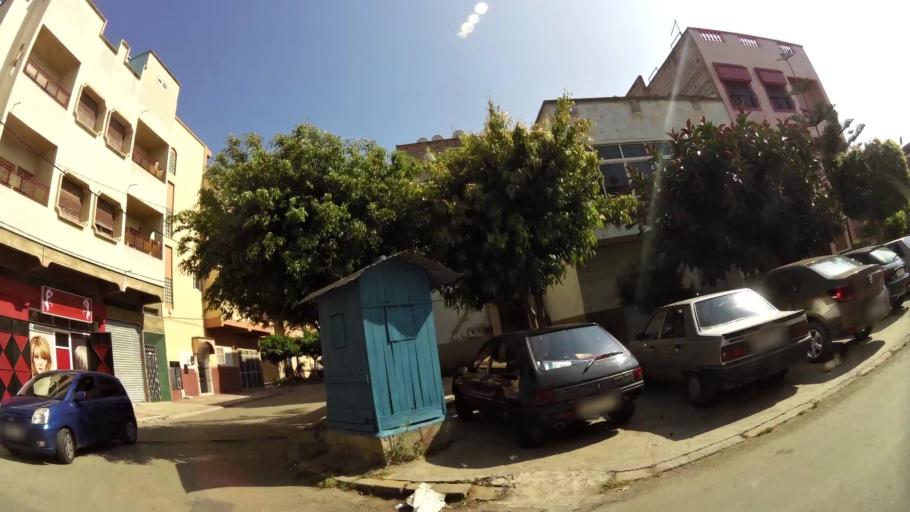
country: MA
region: Rabat-Sale-Zemmour-Zaer
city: Sale
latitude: 34.0418
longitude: -6.7840
